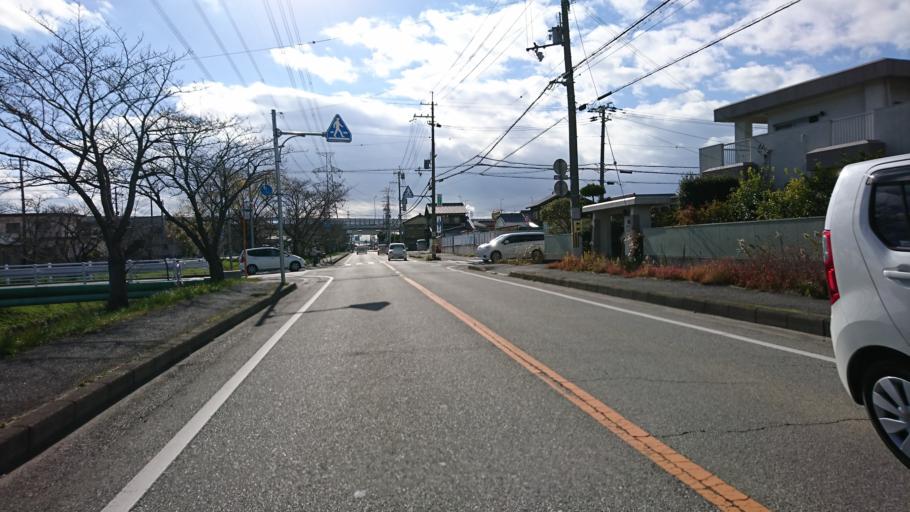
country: JP
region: Hyogo
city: Kakogawacho-honmachi
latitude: 34.7879
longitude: 134.7834
